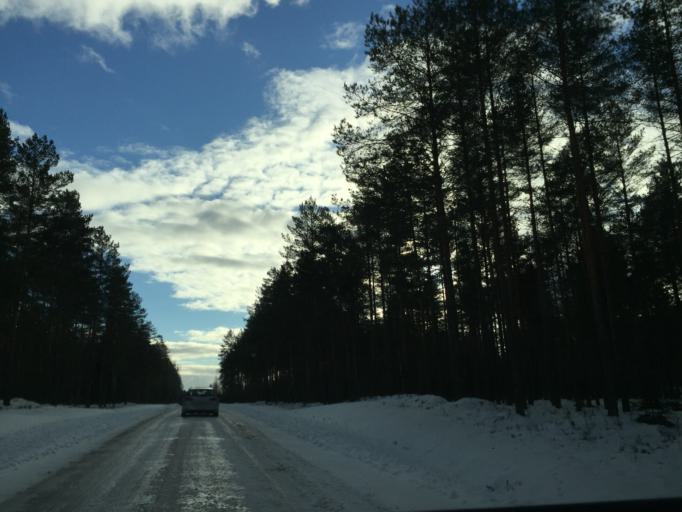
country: LV
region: Ogre
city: Jumprava
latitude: 56.5599
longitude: 24.8549
